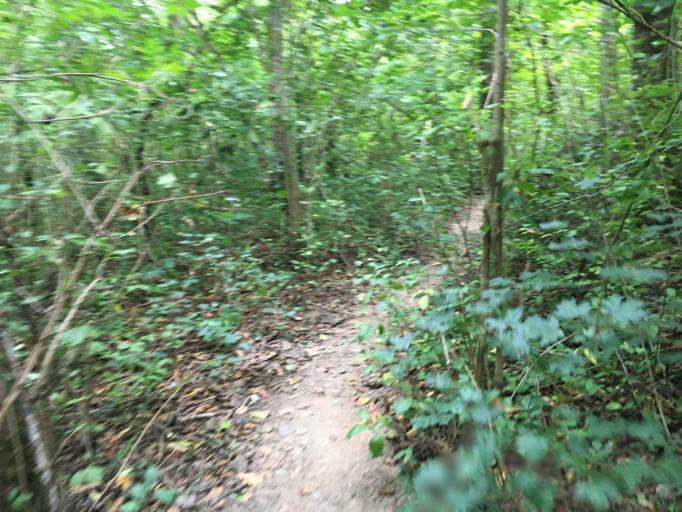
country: RU
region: Krasnodarskiy
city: Tuapse
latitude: 44.2562
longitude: 39.2236
